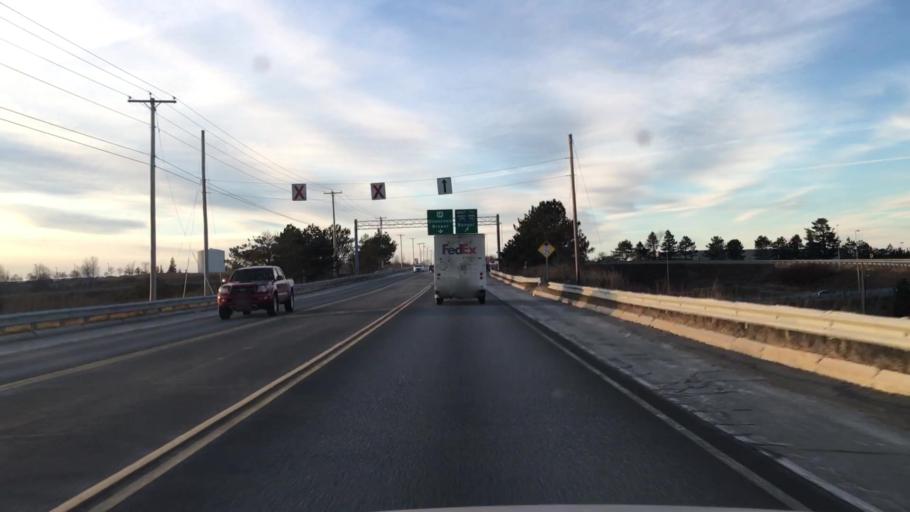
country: US
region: Maine
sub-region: Penobscot County
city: Holden
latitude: 44.7706
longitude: -68.7199
